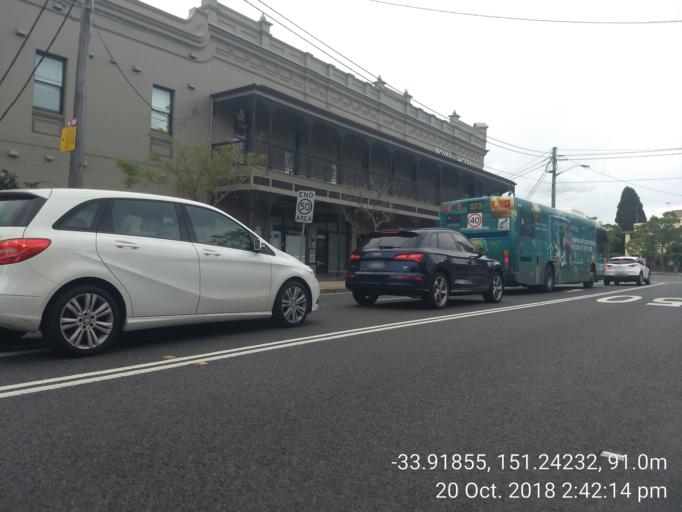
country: AU
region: New South Wales
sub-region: Randwick
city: Randwick
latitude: -33.9186
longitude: 151.2423
